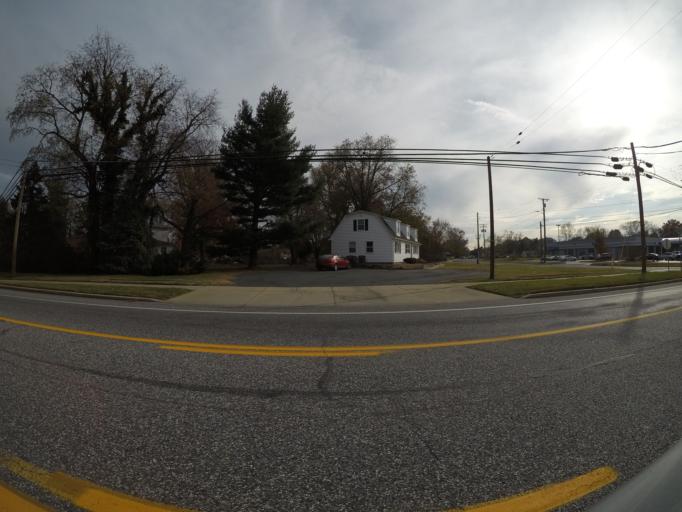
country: US
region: Maryland
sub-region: Harford County
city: Havre de Grace
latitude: 39.5434
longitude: -76.0991
